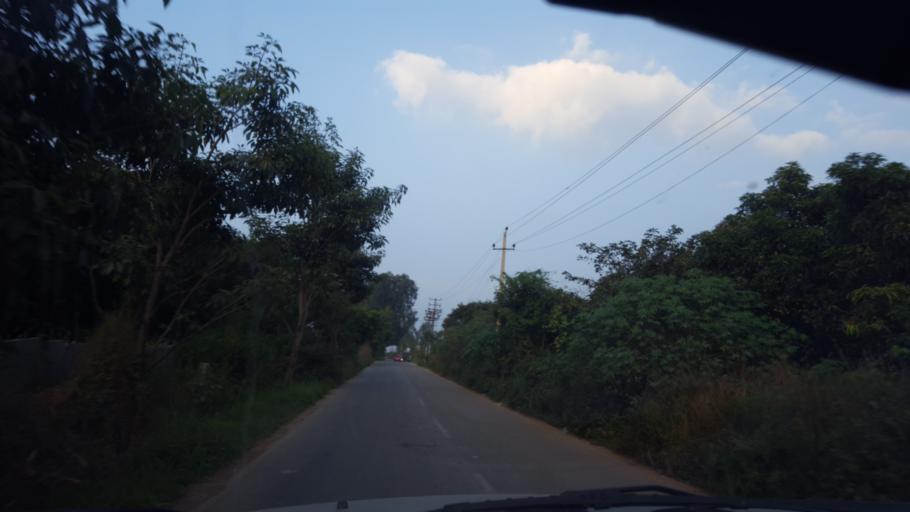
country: IN
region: Karnataka
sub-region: Bangalore Urban
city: Yelahanka
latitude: 13.0575
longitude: 77.6839
